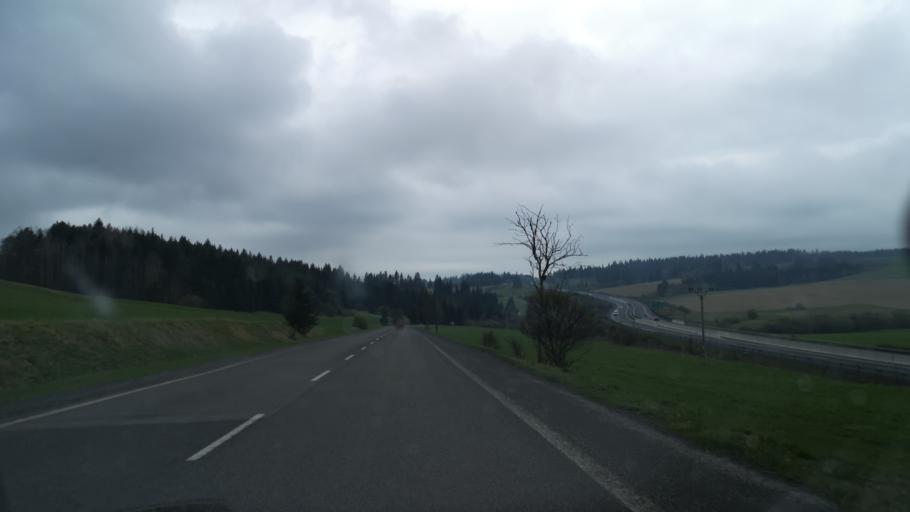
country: SK
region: Zilinsky
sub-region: Okres Liptovsky Mikulas
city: Hybe
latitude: 49.0633
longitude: 19.9533
